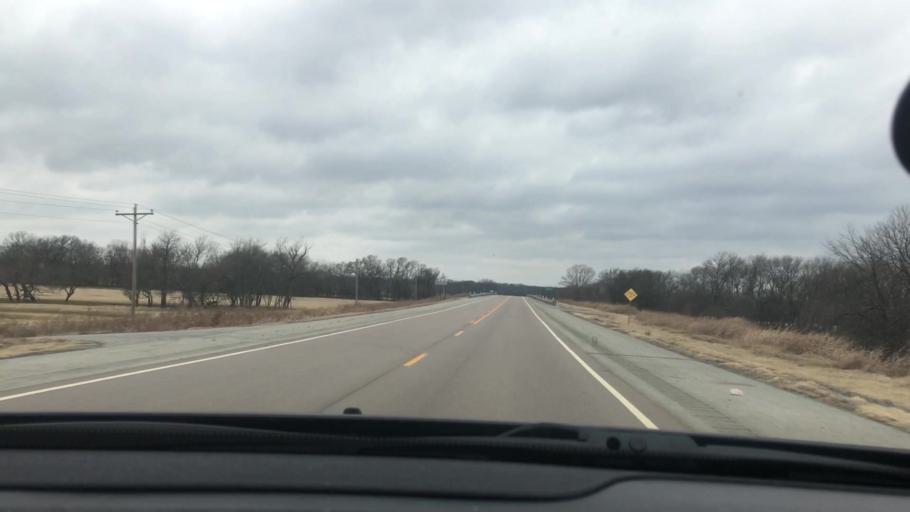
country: US
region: Oklahoma
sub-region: Atoka County
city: Atoka
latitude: 34.3706
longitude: -96.3175
